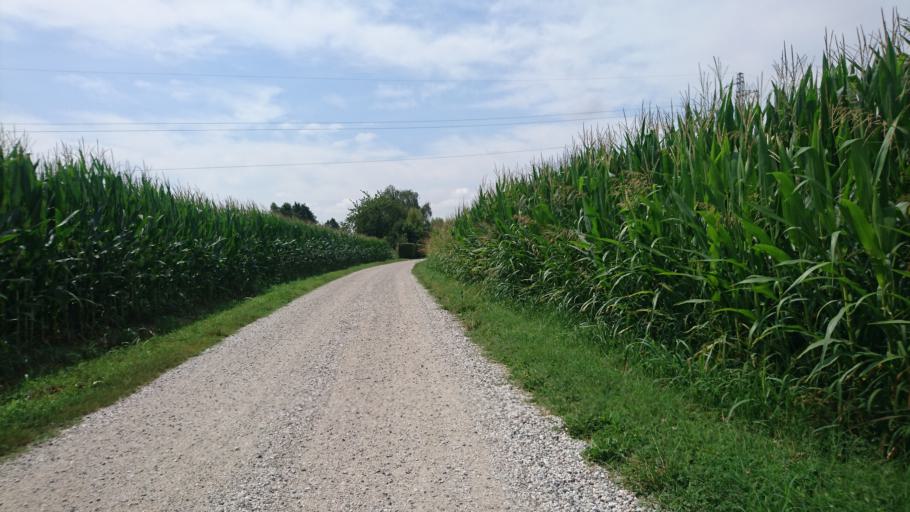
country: IT
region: Veneto
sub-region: Provincia di Padova
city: Sarmeola
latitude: 45.4202
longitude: 11.8464
